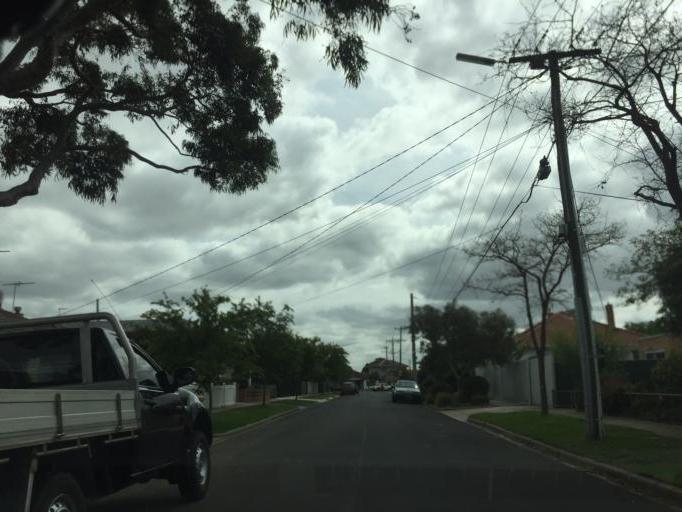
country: AU
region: Victoria
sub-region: Hobsons Bay
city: South Kingsville
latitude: -37.8150
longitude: 144.8636
